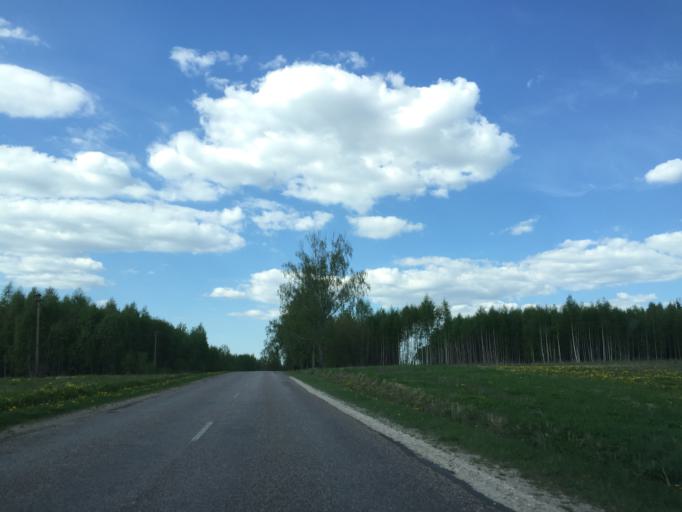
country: LV
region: Limbazu Rajons
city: Limbazi
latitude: 57.4802
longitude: 24.7108
